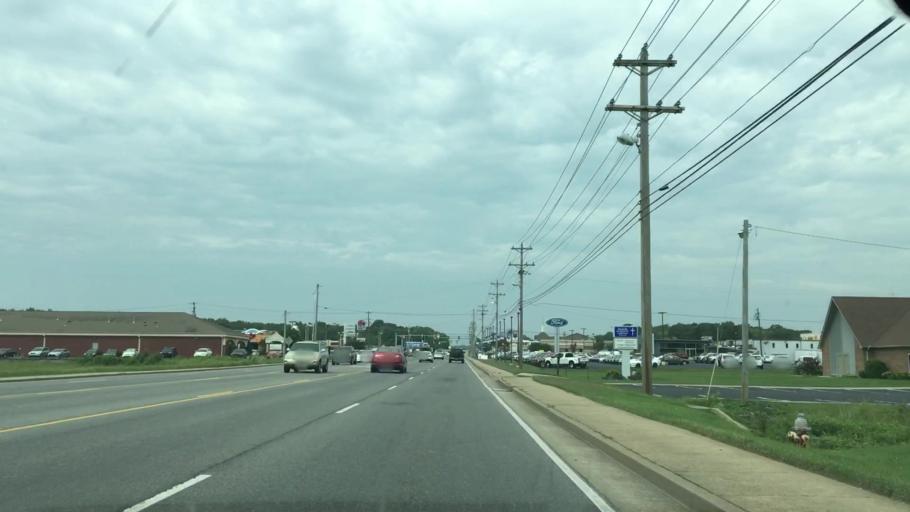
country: US
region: Tennessee
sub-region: Wilson County
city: Lebanon
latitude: 36.2205
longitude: -86.3420
